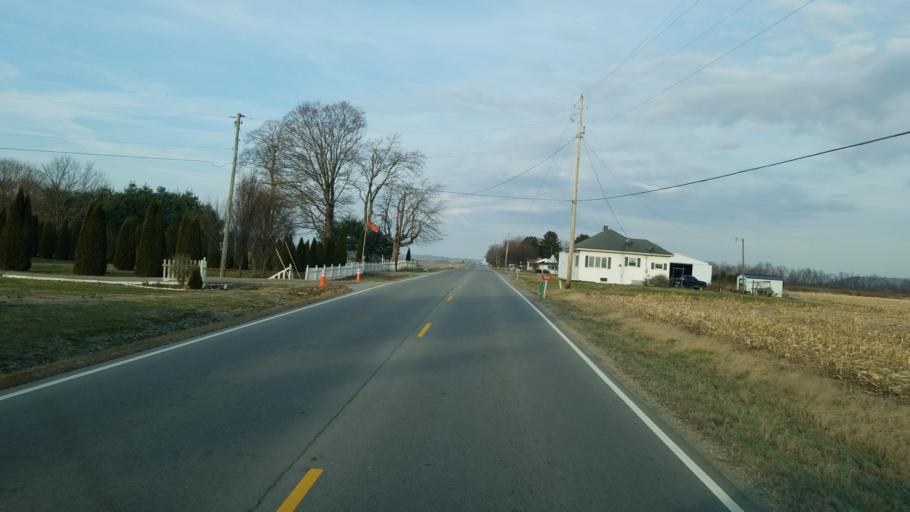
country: US
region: Ohio
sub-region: Ross County
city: Chillicothe
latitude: 39.2917
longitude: -82.8798
